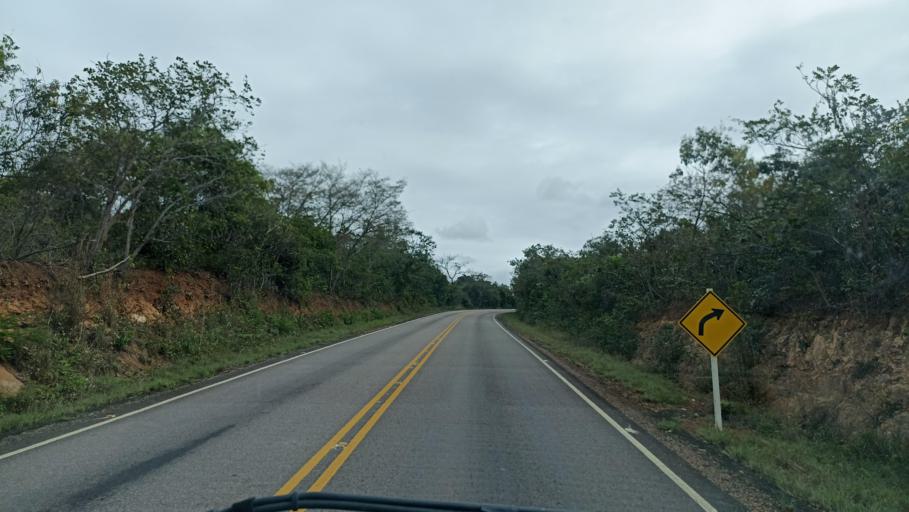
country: BR
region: Bahia
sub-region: Andarai
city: Vera Cruz
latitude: -12.9280
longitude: -41.2344
